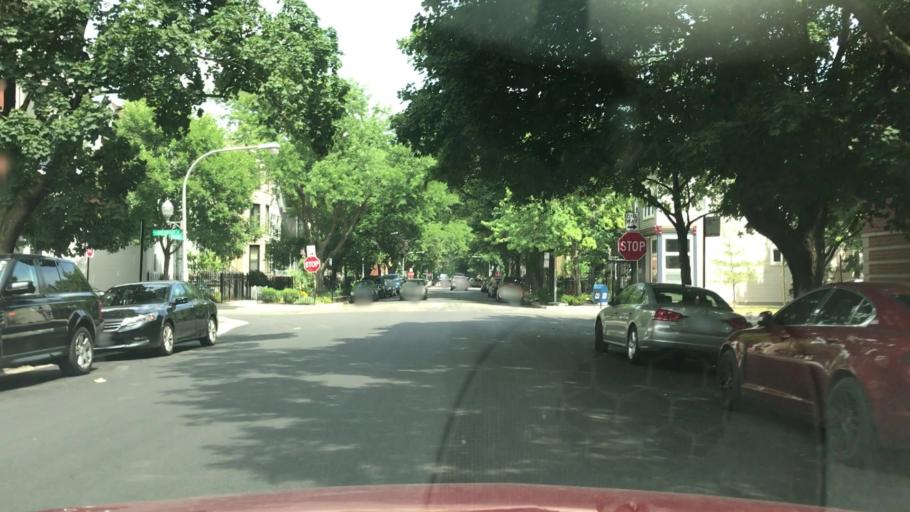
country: US
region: Illinois
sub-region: Cook County
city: Chicago
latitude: 41.9340
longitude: -87.6585
